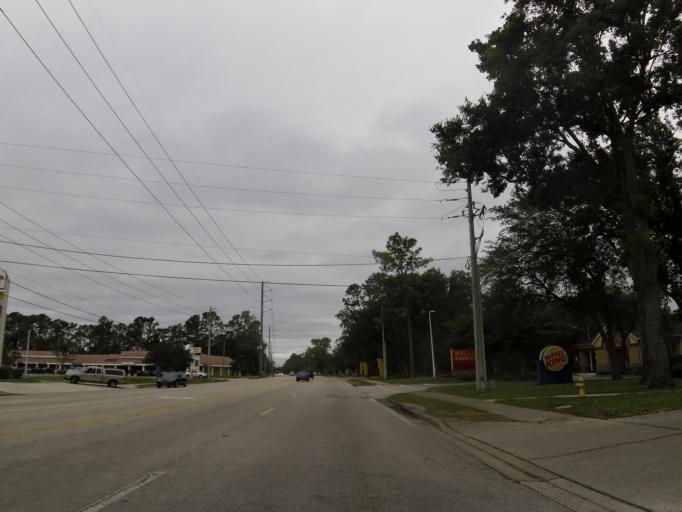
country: US
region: Florida
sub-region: Saint Johns County
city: Fruit Cove
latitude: 30.1742
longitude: -81.6037
